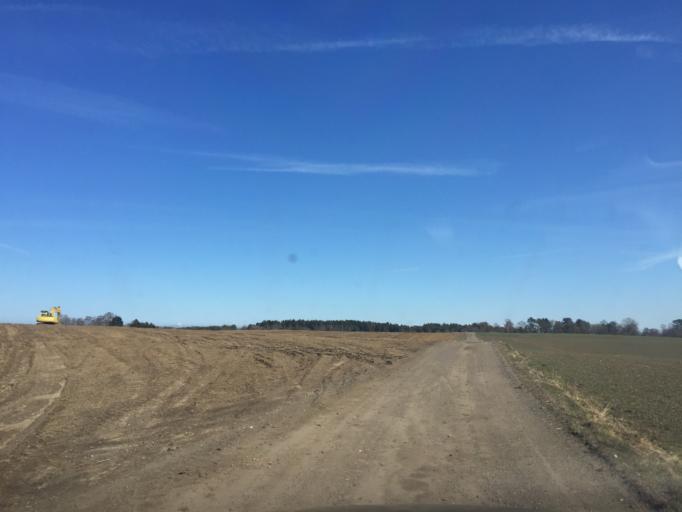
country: DK
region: Capital Region
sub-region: Helsingor Kommune
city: Hornbaek
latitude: 56.0771
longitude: 12.3943
